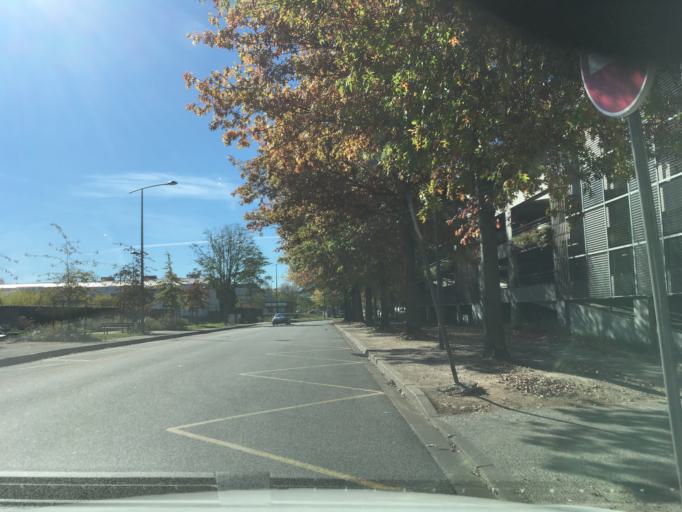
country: FR
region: Aquitaine
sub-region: Departement des Pyrenees-Atlantiques
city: Pau
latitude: 43.3171
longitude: -0.3562
